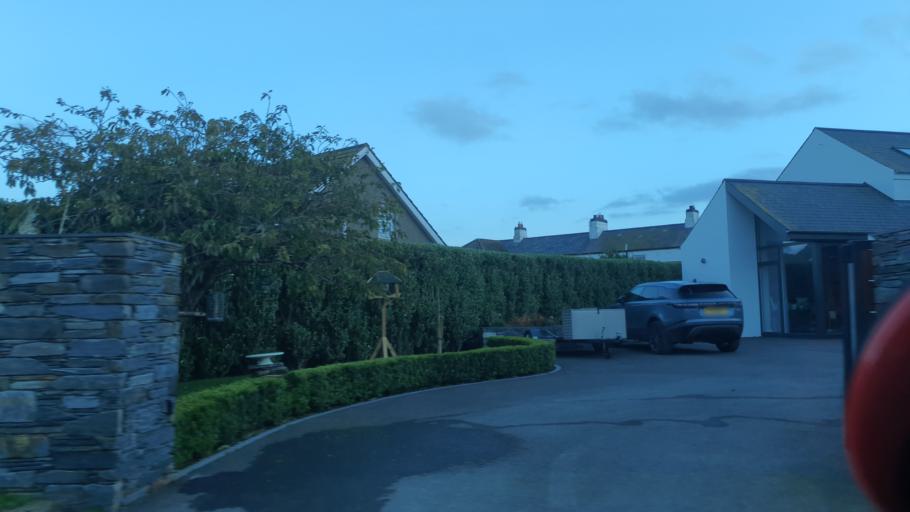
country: IE
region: Leinster
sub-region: Lu
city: Carlingford
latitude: 54.0410
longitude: -6.1059
